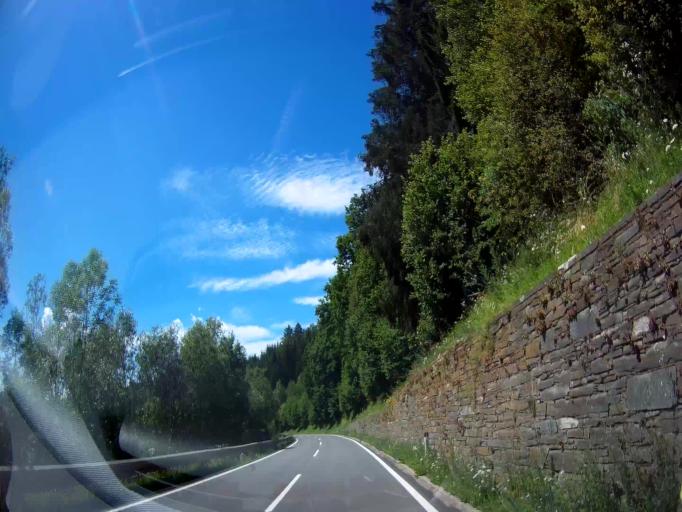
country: AT
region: Carinthia
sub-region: Politischer Bezirk Sankt Veit an der Glan
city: Glodnitz
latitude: 46.8512
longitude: 14.1648
